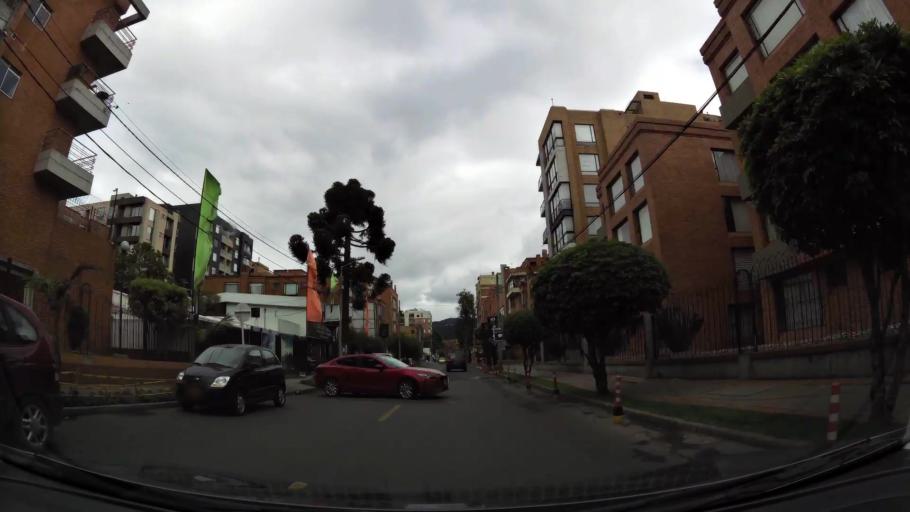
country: CO
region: Bogota D.C.
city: Barrio San Luis
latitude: 4.6831
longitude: -74.0564
